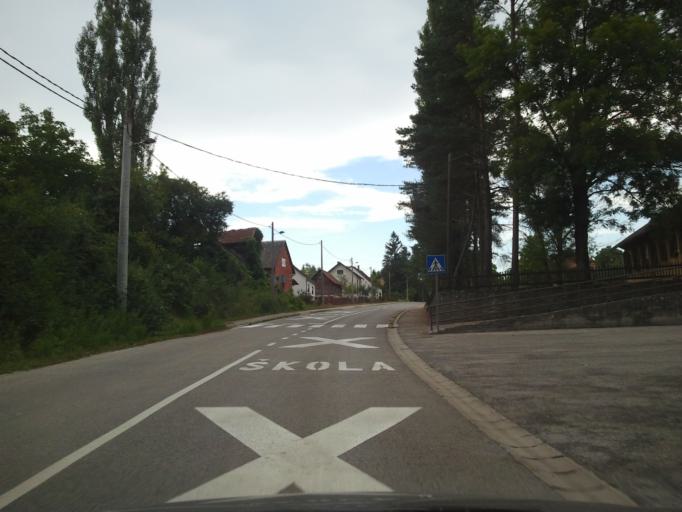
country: HR
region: Sisacko-Moslavacka
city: Glina
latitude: 45.4817
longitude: 15.9941
